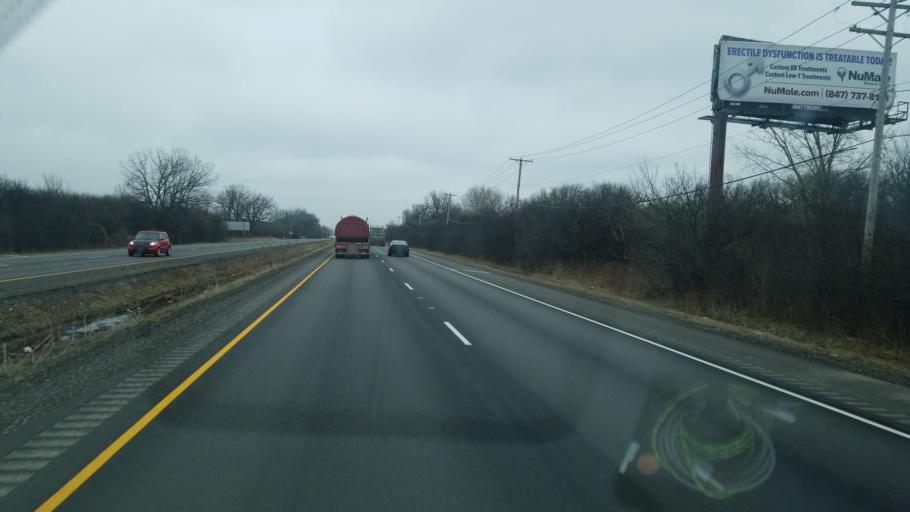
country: US
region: Illinois
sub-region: Lake County
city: Park City
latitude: 42.3217
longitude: -87.8811
